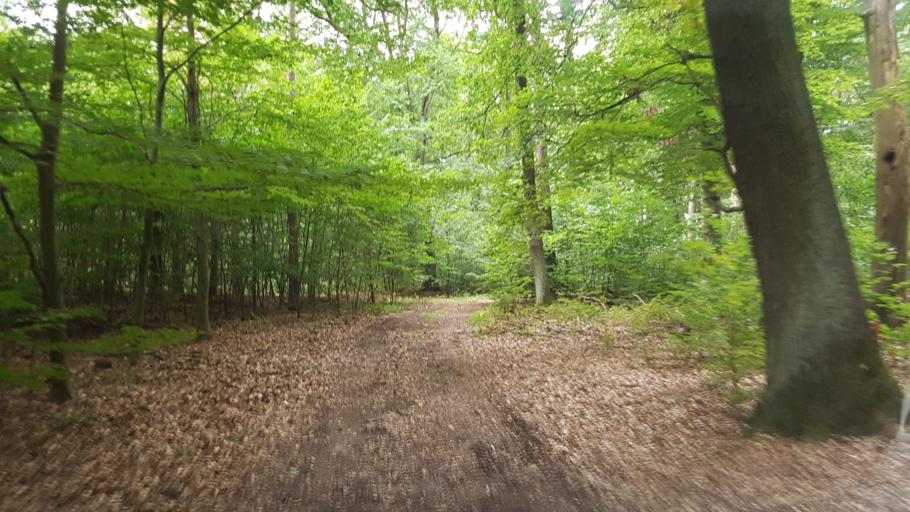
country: DE
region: Brandenburg
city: Schonborn
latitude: 51.6082
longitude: 13.5202
